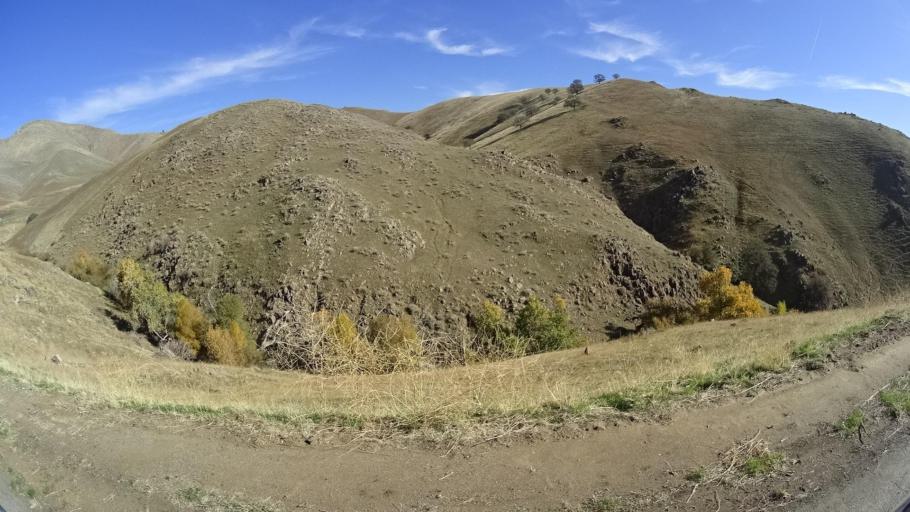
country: US
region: California
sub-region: Kern County
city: Arvin
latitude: 35.4128
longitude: -118.7469
